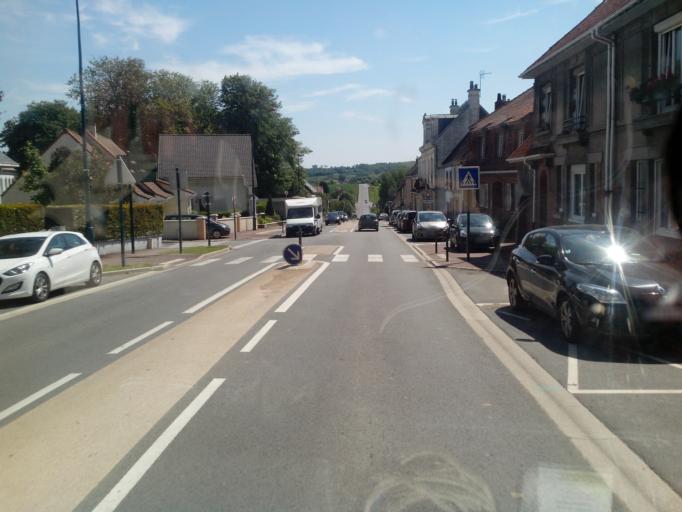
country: FR
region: Nord-Pas-de-Calais
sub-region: Departement du Pas-de-Calais
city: Samer
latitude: 50.6377
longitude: 1.7430
